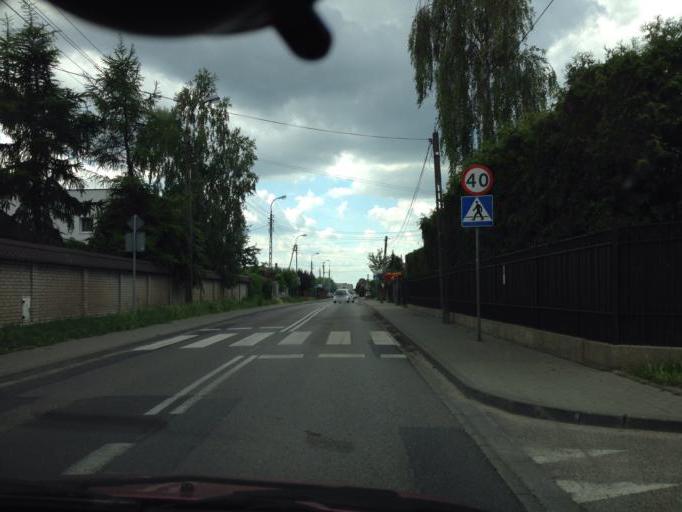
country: PL
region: Masovian Voivodeship
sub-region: Warszawa
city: Bemowo
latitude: 52.2422
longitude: 20.8855
